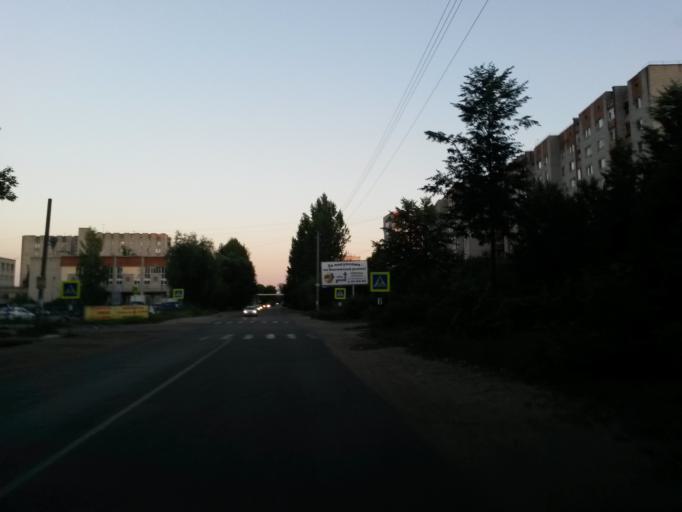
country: RU
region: Jaroslavl
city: Yaroslavl
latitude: 57.5755
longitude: 39.9287
